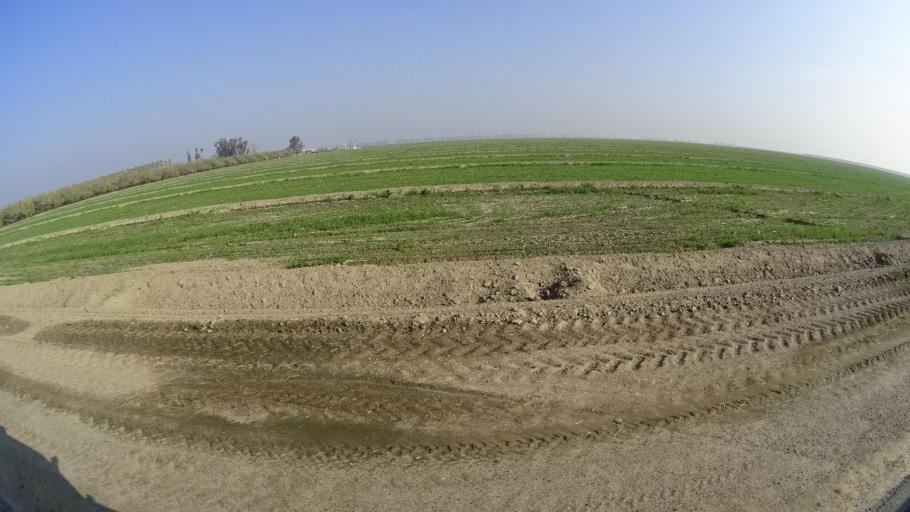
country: US
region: California
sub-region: Kern County
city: Greenfield
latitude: 35.1887
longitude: -119.0446
